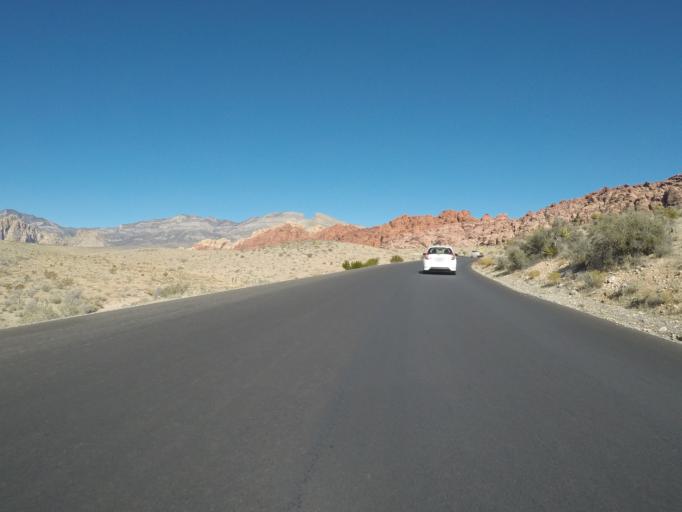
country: US
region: Nevada
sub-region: Clark County
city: Summerlin South
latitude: 36.1399
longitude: -115.4275
